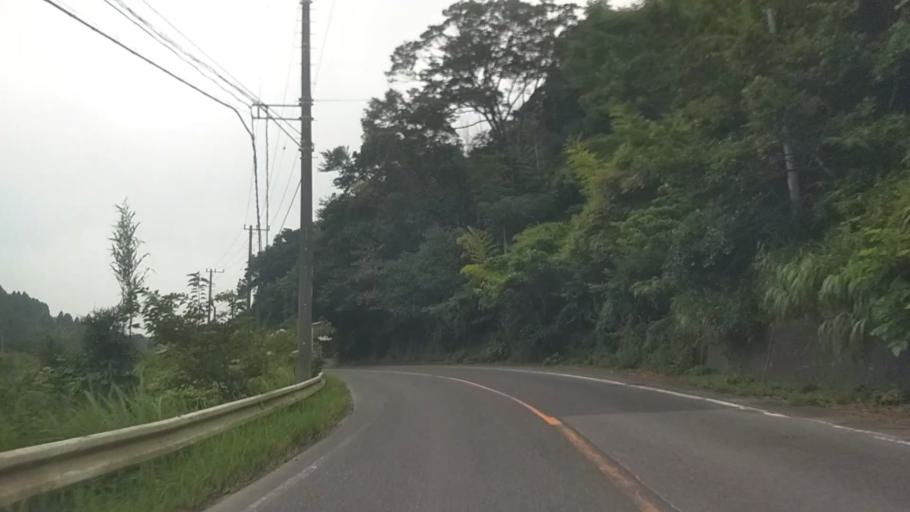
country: JP
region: Chiba
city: Tateyama
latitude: 35.1446
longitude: 139.8670
